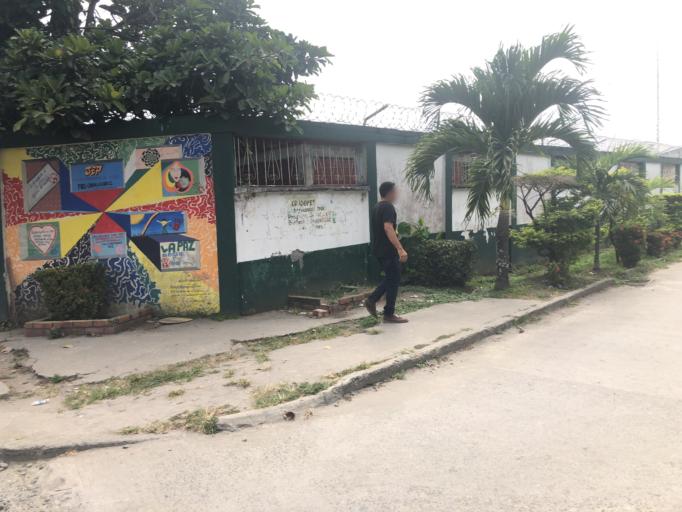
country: CO
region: Narino
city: Tumaco
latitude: 1.8181
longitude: -78.7496
